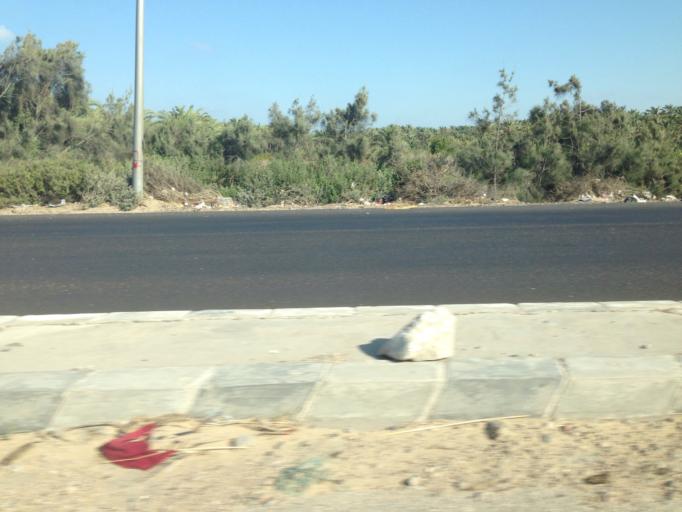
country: EG
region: Al Buhayrah
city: Idku
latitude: 31.2962
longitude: 30.2604
